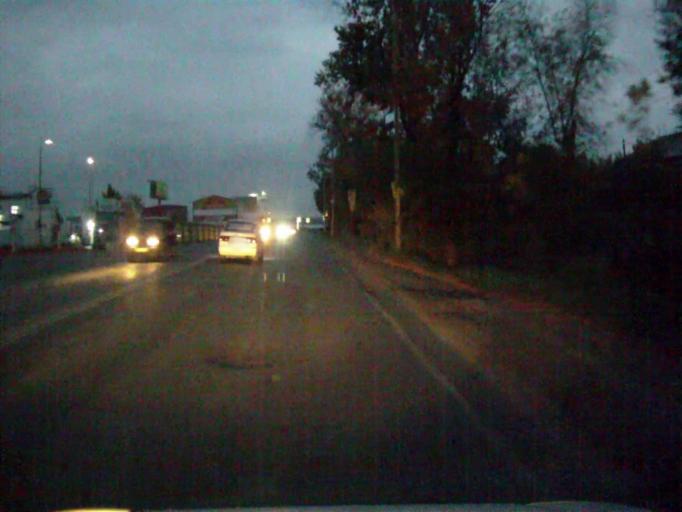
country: RU
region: Chelyabinsk
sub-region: Gorod Chelyabinsk
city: Chelyabinsk
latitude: 55.1504
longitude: 61.3033
